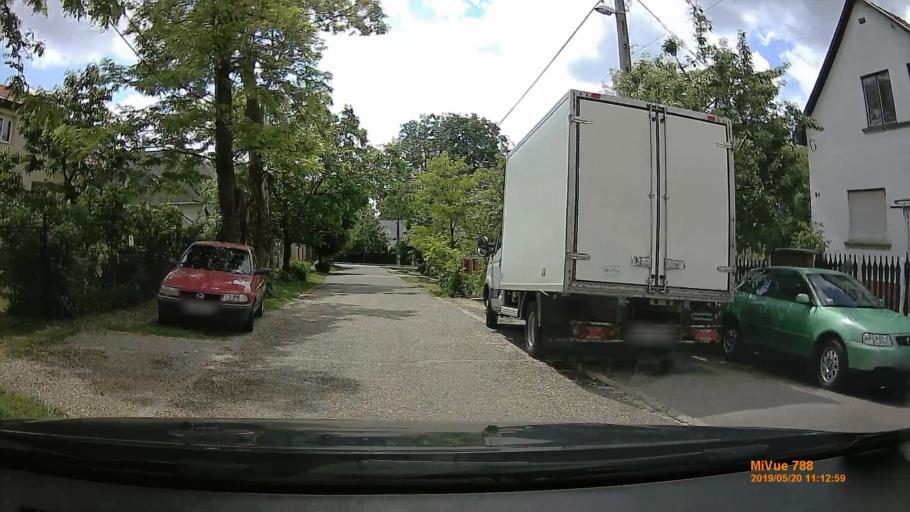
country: HU
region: Pest
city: Ecser
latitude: 47.4610
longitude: 19.2980
